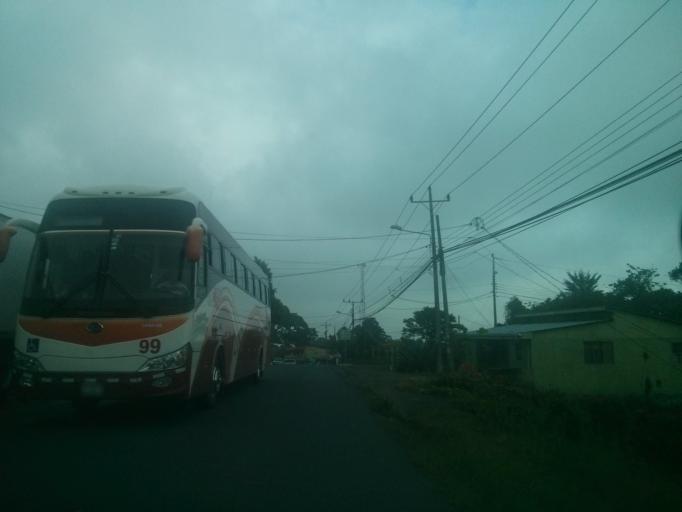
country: CR
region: Cartago
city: Cot
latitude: 9.8847
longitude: -83.8106
